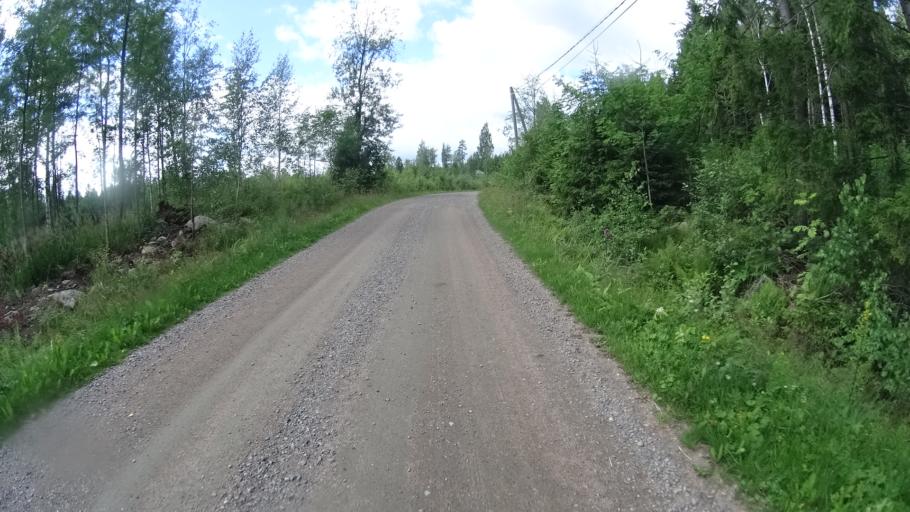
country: FI
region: Uusimaa
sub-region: Helsinki
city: Karkkila
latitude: 60.5967
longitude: 24.2180
